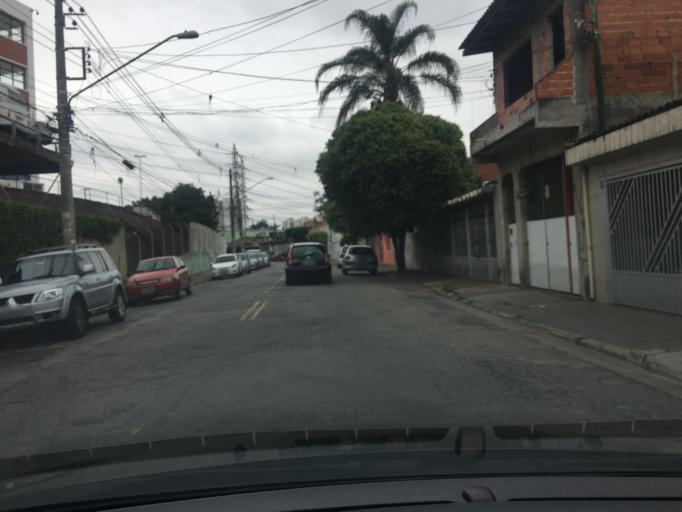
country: BR
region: Sao Paulo
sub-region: Guarulhos
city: Guarulhos
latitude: -23.4922
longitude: -46.5477
